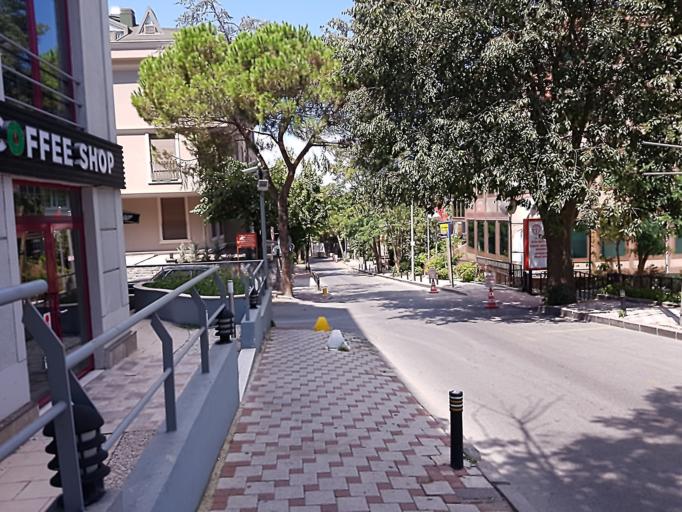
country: TR
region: Istanbul
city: Sisli
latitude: 41.0698
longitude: 29.0100
